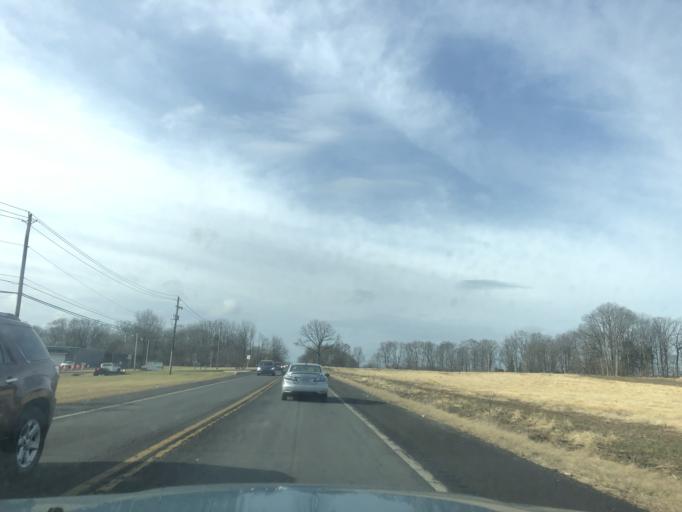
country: US
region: Pennsylvania
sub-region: Bucks County
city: Quakertown
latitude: 40.4414
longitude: -75.3871
